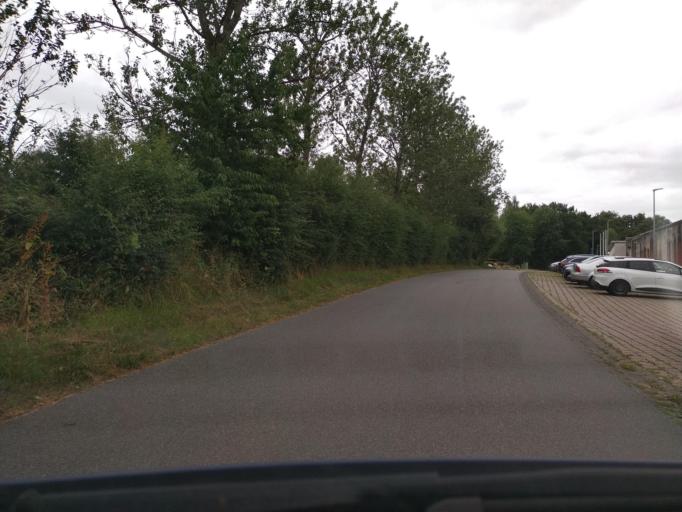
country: DE
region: Schleswig-Holstein
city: Schuby
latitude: 54.5167
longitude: 9.5176
